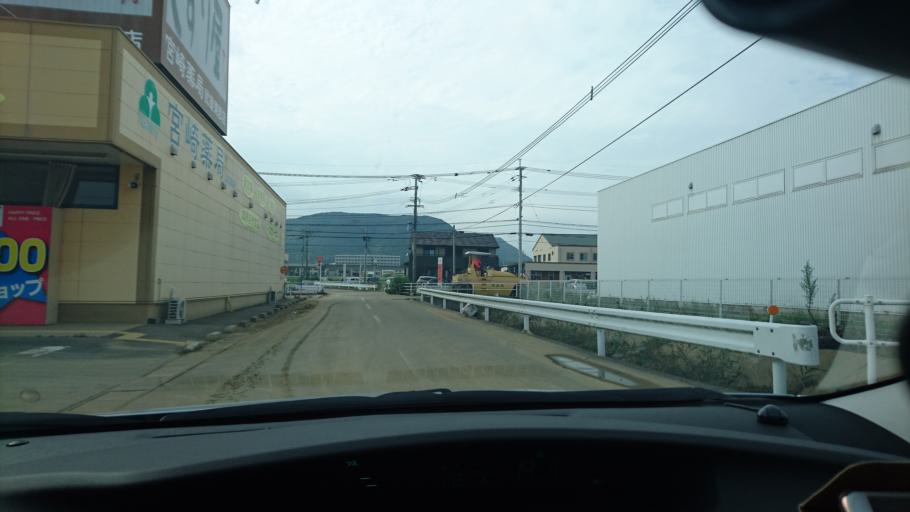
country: JP
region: Saga Prefecture
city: Takeocho-takeo
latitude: 33.1982
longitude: 130.0335
